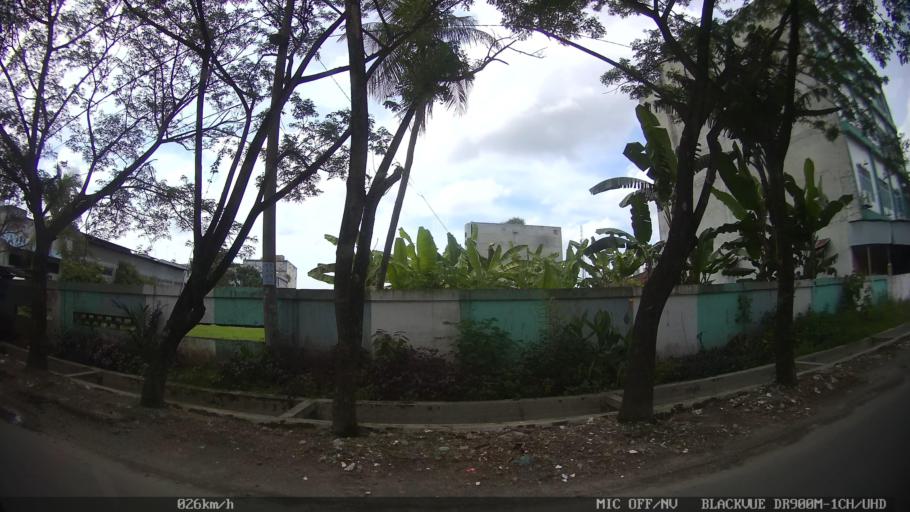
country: ID
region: North Sumatra
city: Percut
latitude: 3.5668
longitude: 98.8749
